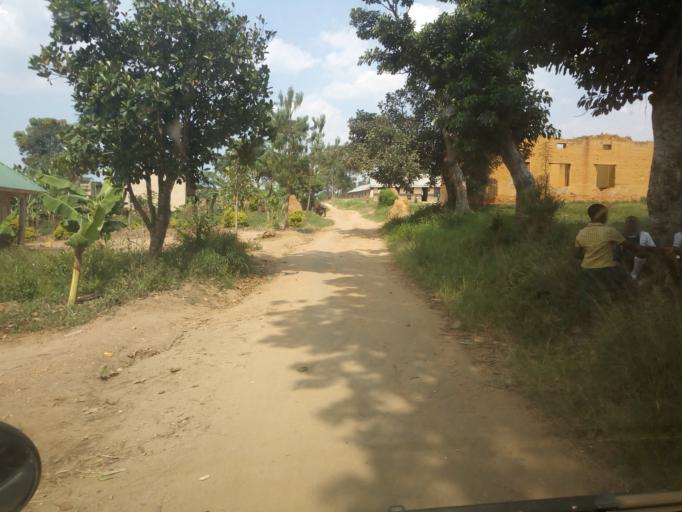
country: UG
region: Western Region
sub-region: Kanungu District
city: Ntungamo
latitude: -0.7913
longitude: 29.6593
